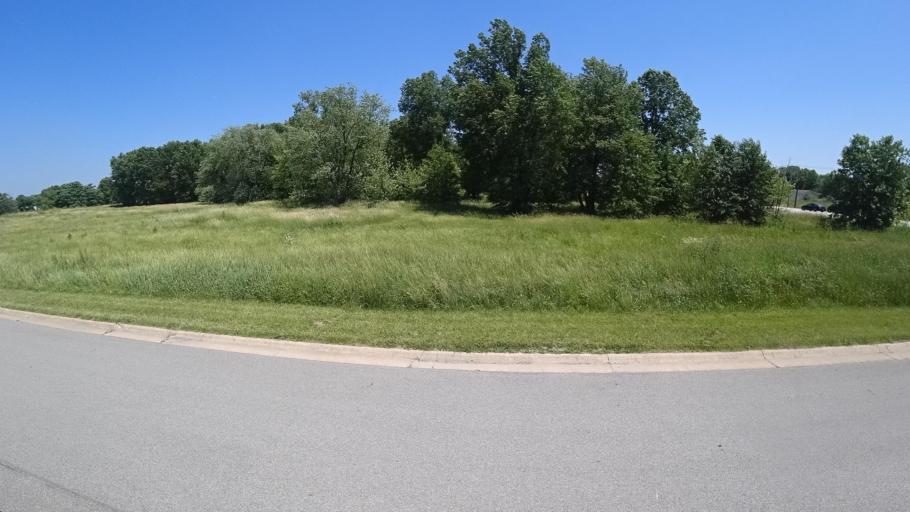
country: US
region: Indiana
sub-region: Porter County
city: Burns Harbor
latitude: 41.6033
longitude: -87.1190
